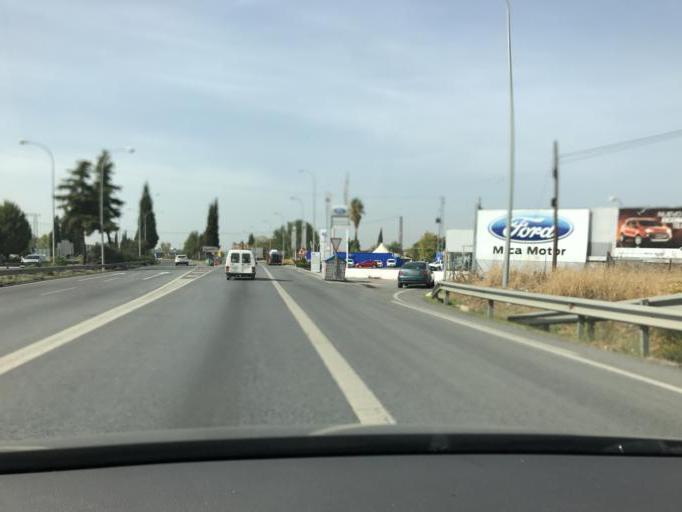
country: ES
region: Andalusia
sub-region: Provincia de Granada
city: Maracena
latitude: 37.1982
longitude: -3.6422
